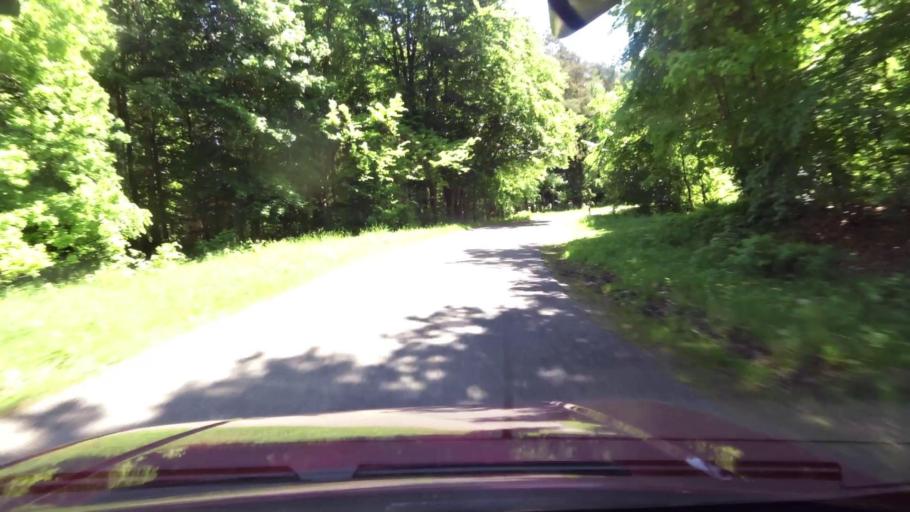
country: PL
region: West Pomeranian Voivodeship
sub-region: Powiat koszalinski
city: Bobolice
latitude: 54.0285
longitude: 16.6389
